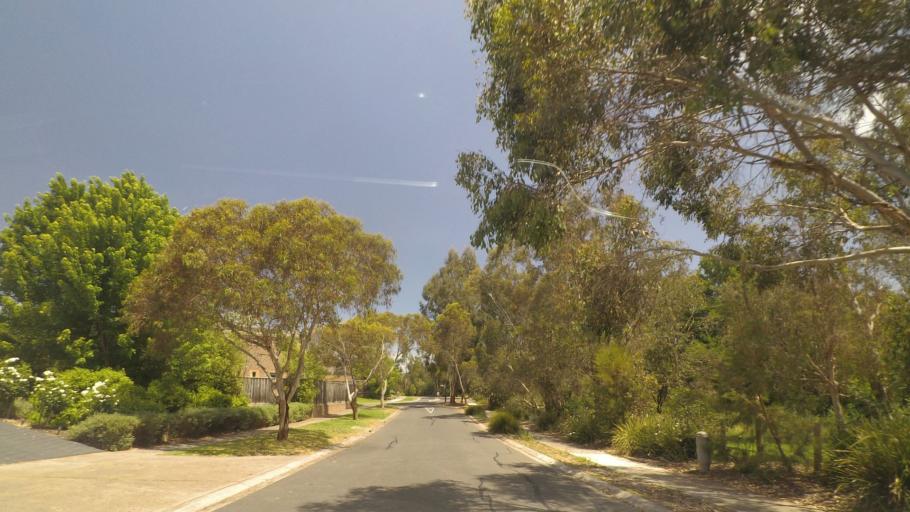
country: AU
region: Victoria
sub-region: Maroondah
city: Croydon North
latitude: -37.7582
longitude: 145.2937
